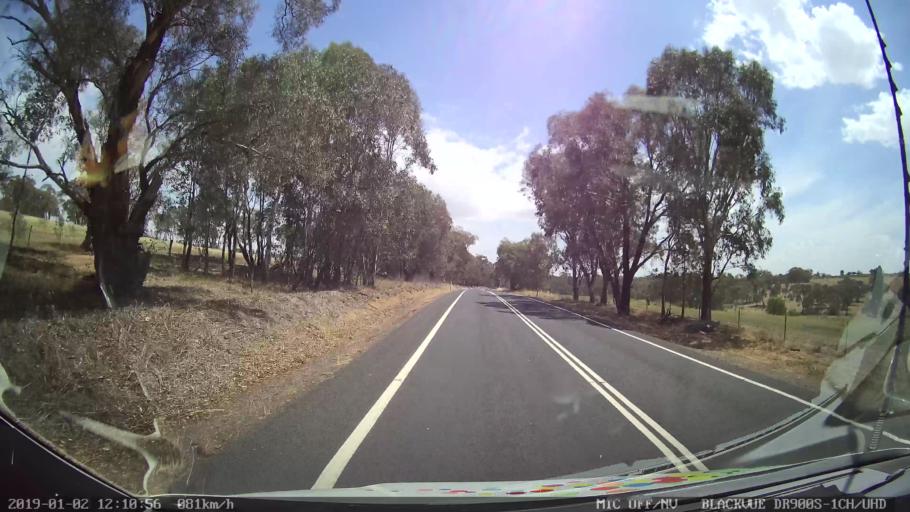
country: AU
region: New South Wales
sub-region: Young
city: Young
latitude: -34.4550
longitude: 148.2598
